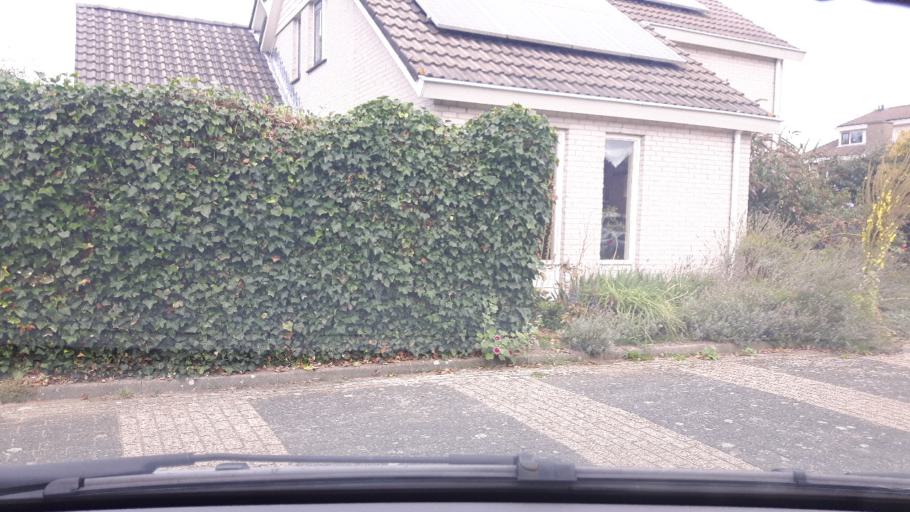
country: NL
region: Gelderland
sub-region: Gemeente Duiven
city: Duiven
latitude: 51.9524
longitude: 6.0047
